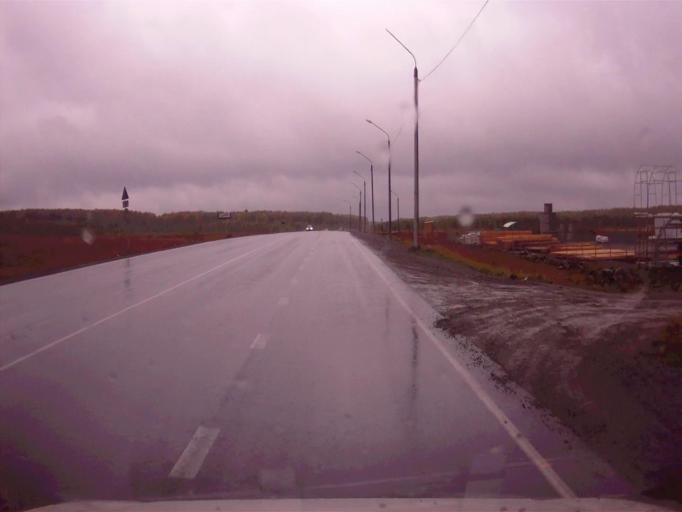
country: RU
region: Chelyabinsk
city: Tayginka
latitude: 55.5010
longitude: 60.6365
